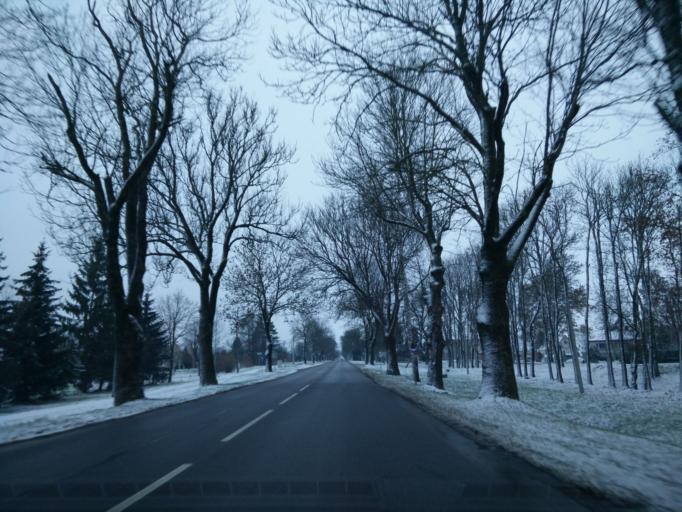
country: LT
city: Kelme
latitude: 55.6247
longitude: 22.9219
